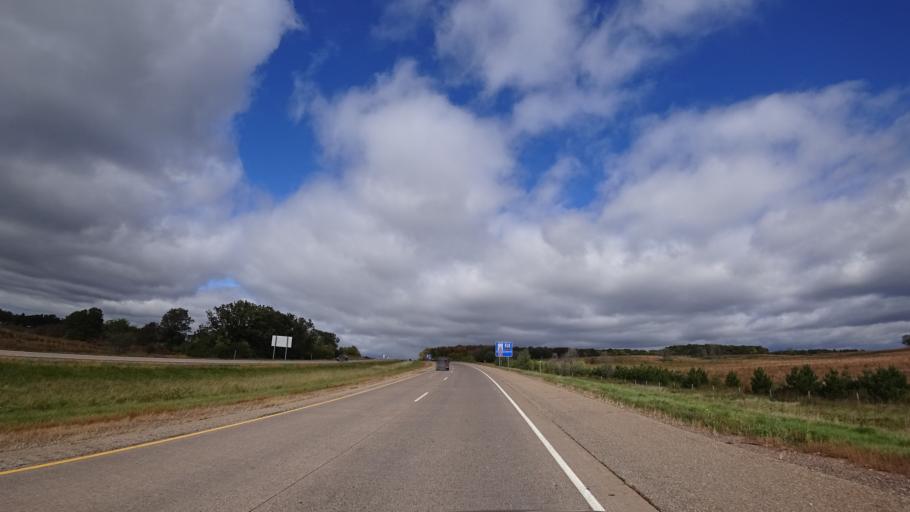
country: US
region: Wisconsin
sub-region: Chippewa County
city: Chippewa Falls
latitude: 44.9032
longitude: -91.3729
